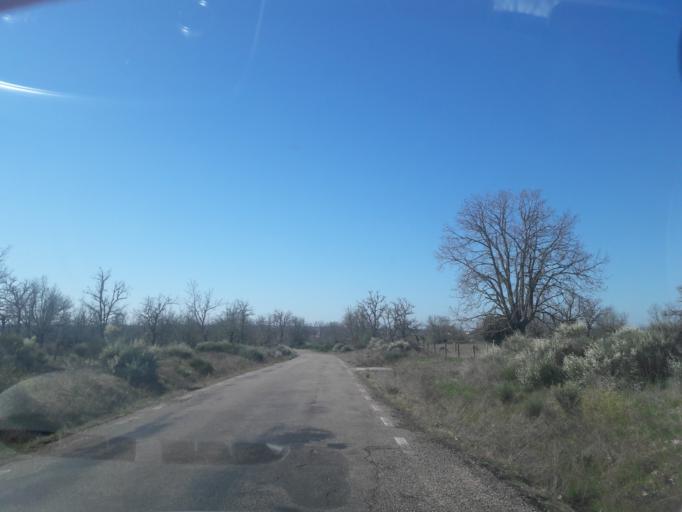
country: ES
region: Castille and Leon
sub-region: Provincia de Salamanca
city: Valsalabroso
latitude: 41.1131
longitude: -6.4835
